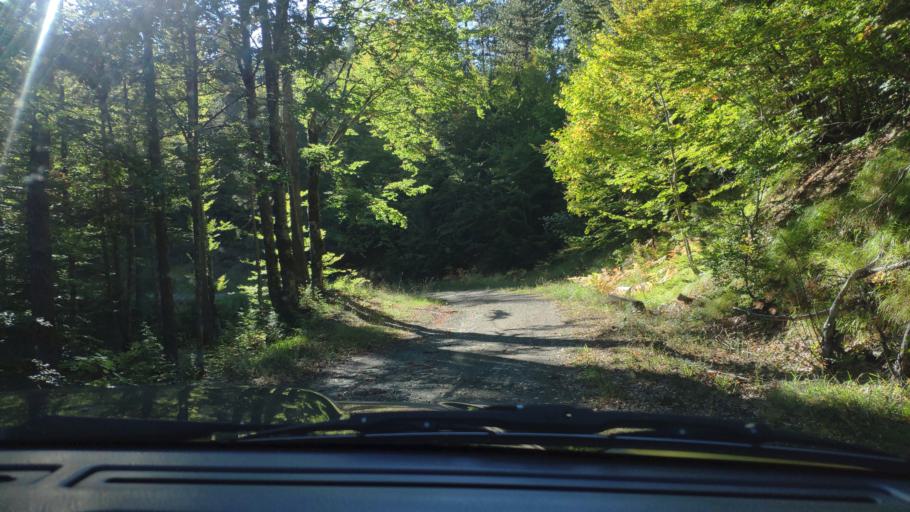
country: AL
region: Korce
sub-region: Rrethi i Devollit
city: Miras
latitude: 40.3667
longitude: 20.8986
